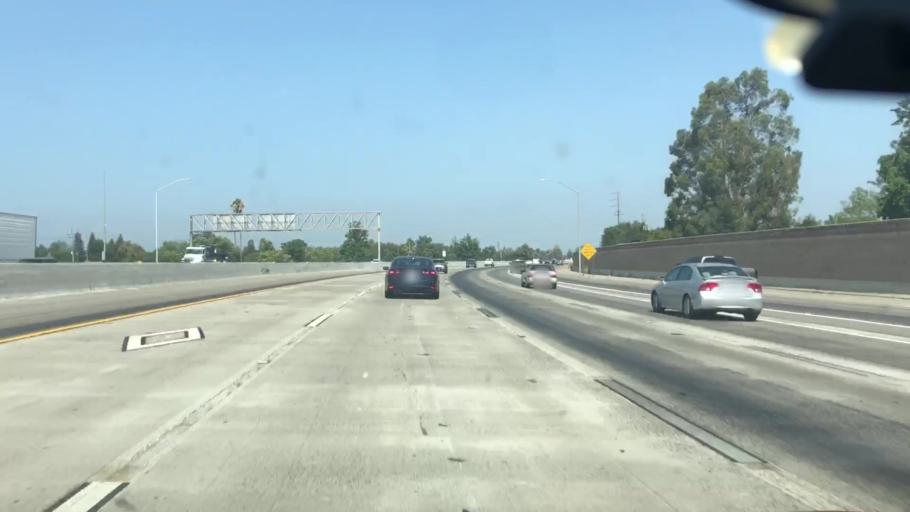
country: US
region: California
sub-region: San Joaquin County
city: Country Club
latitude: 37.9584
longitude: -121.3316
